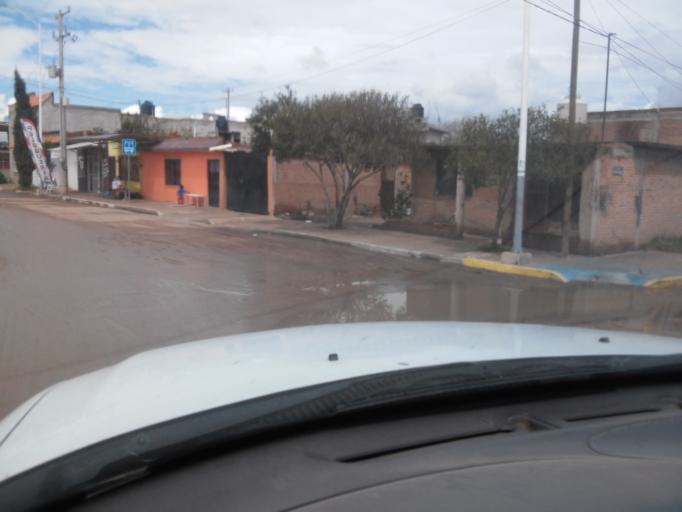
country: MX
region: Durango
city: Victoria de Durango
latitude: 24.0181
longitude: -104.6131
